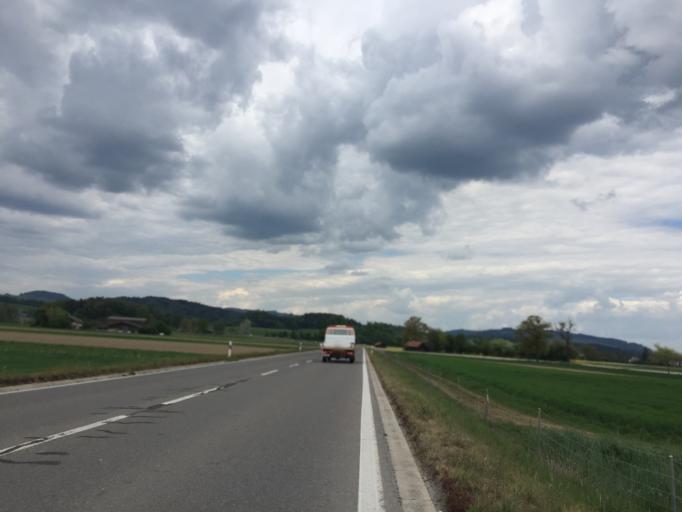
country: CH
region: Bern
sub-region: Thun District
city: Uttigen
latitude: 46.7825
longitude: 7.5838
